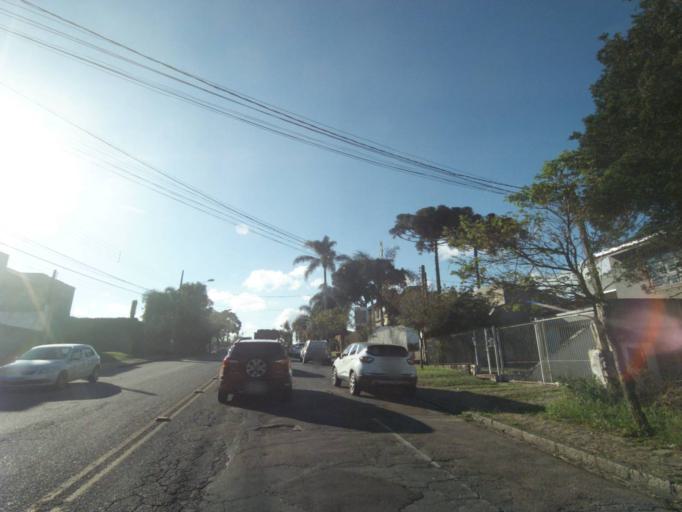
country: BR
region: Parana
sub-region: Curitiba
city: Curitiba
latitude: -25.3942
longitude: -49.2525
